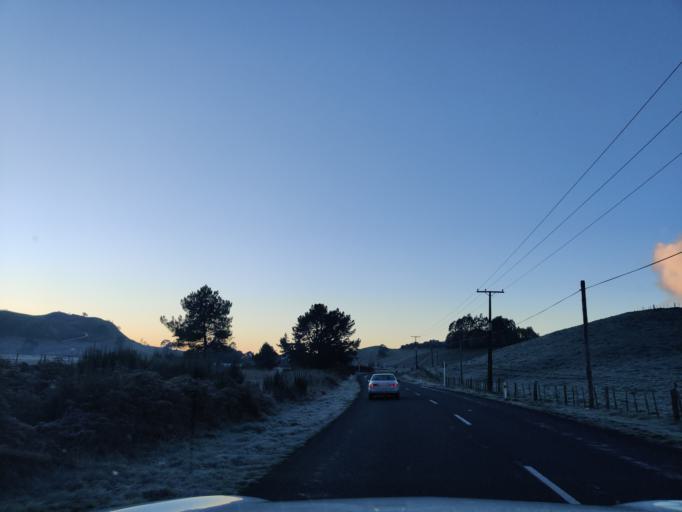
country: NZ
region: Waikato
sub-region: Taupo District
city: Taupo
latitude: -38.5873
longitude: 176.0272
